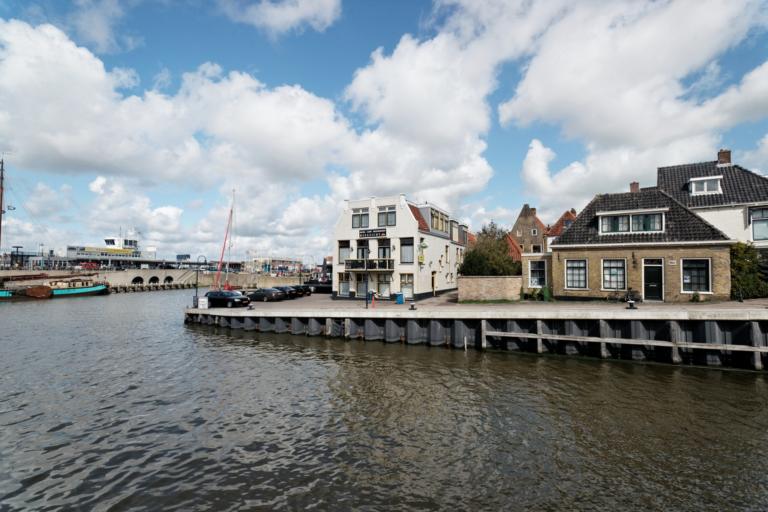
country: NL
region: Friesland
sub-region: Gemeente Harlingen
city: Harlingen
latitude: 53.1751
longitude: 5.4130
